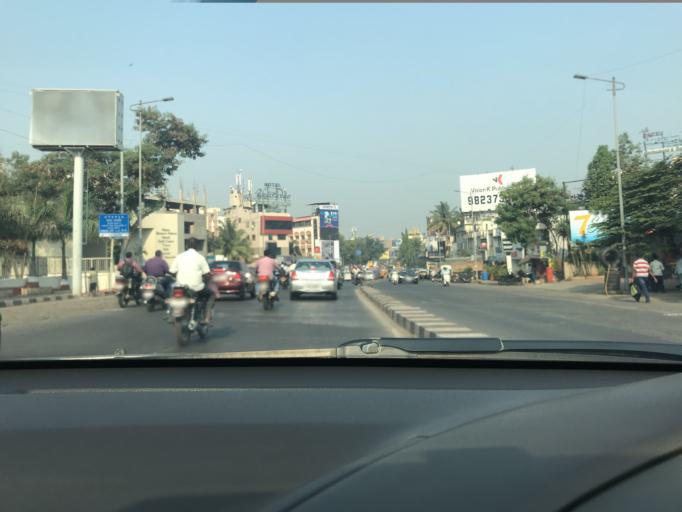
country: IN
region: Maharashtra
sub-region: Pune Division
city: Khadki
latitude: 18.5515
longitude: 73.8045
